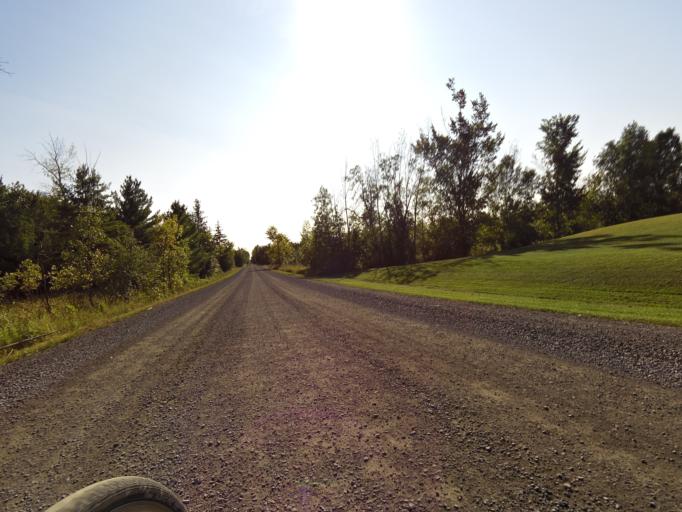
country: CA
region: Ontario
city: Bells Corners
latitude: 45.4849
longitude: -76.0381
